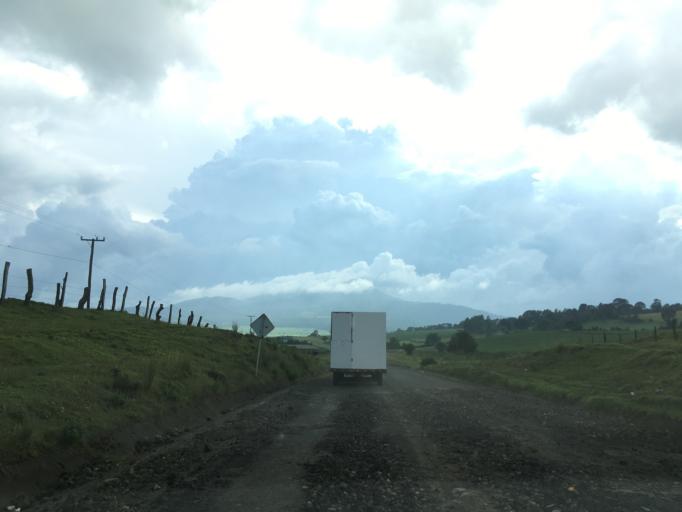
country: MX
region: Michoacan
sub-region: Nahuatzen
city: Sevina
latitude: 19.6373
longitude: -101.8332
